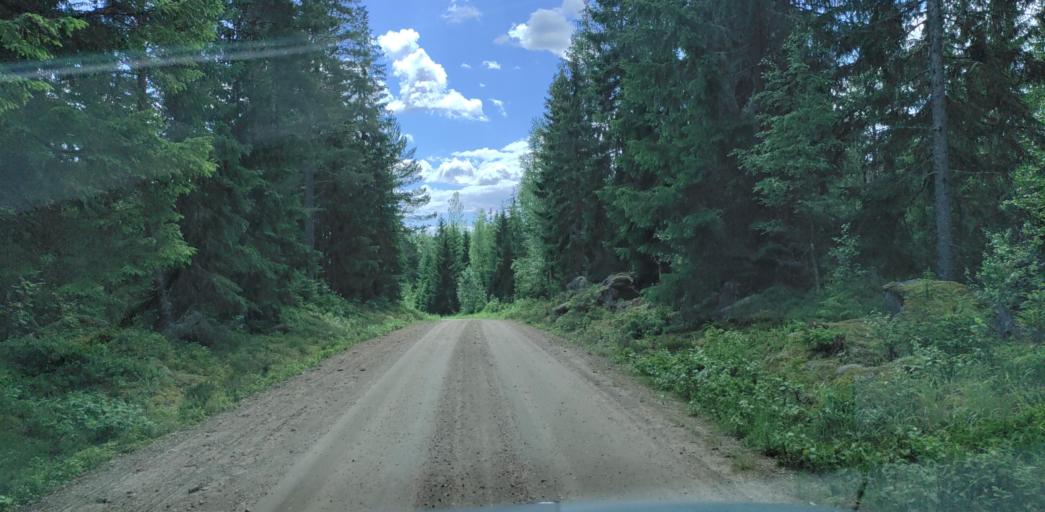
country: SE
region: Vaermland
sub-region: Hagfors Kommun
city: Ekshaerad
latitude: 60.1007
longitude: 13.3179
